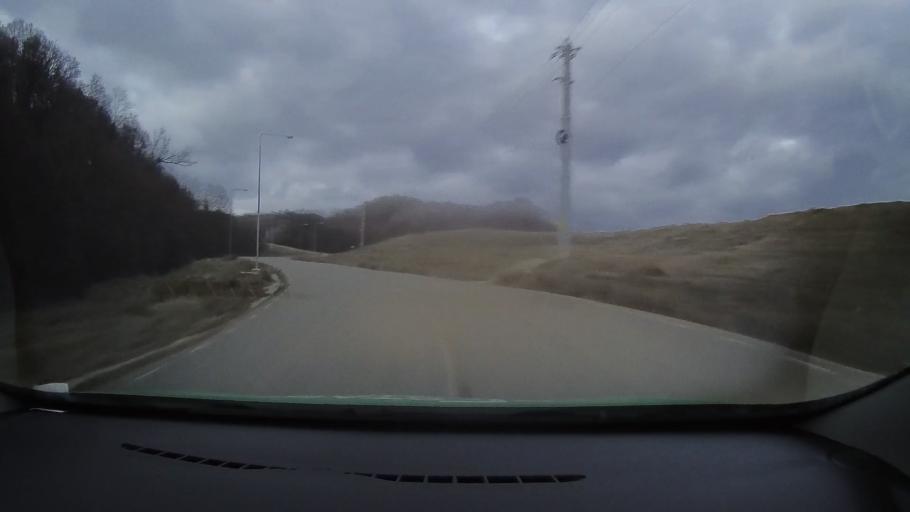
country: RO
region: Prahova
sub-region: Comuna Adunati
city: Adunati
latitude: 45.1246
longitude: 25.6109
